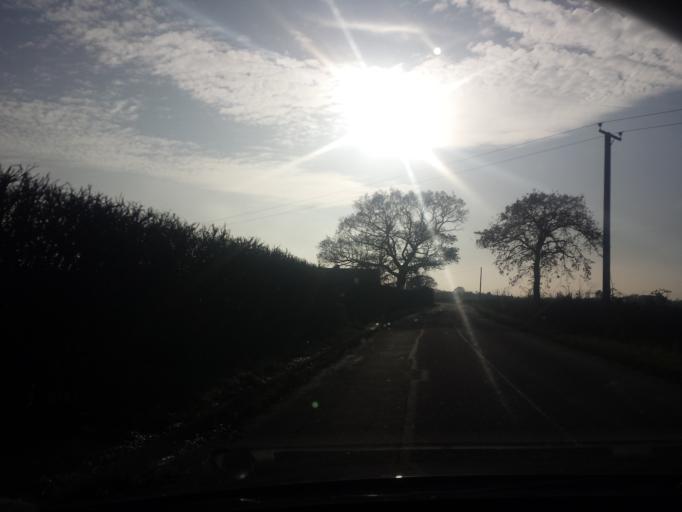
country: GB
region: England
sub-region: Essex
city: Little Clacton
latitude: 51.8256
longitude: 1.1121
